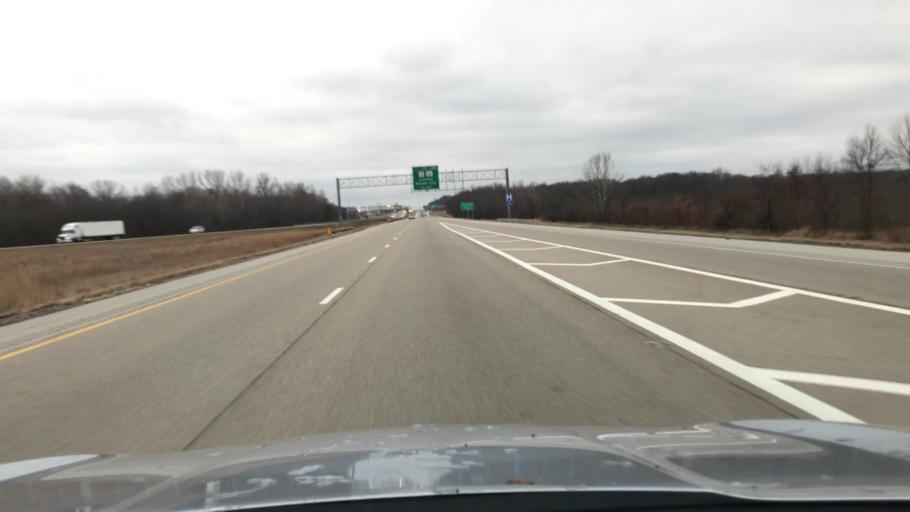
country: US
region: Illinois
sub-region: Logan County
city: Lincoln
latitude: 40.1722
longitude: -89.4181
